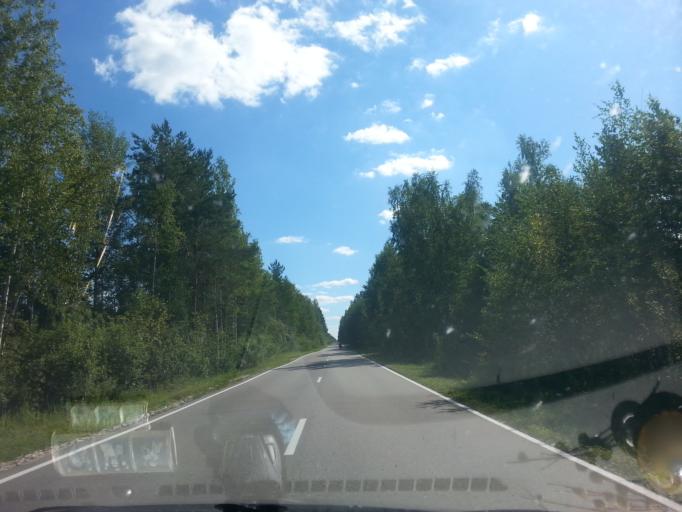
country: RU
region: Vladimir
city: Galitsy
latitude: 56.1256
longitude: 42.8732
